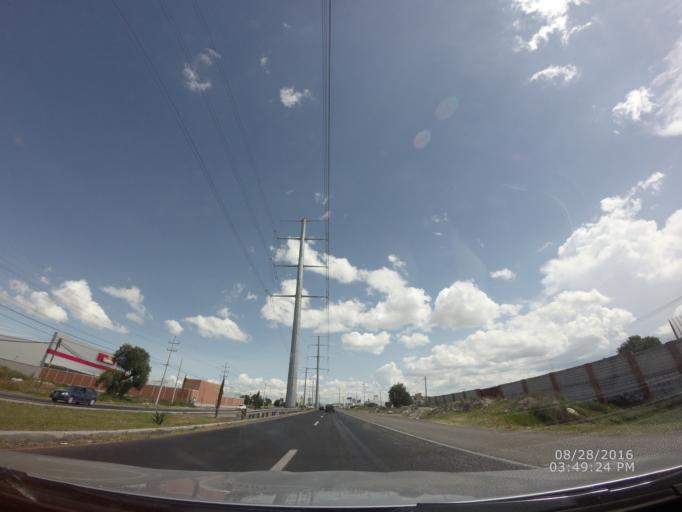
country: MX
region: Hidalgo
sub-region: Mineral de la Reforma
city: Los Tuzos
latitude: 20.0442
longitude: -98.7354
